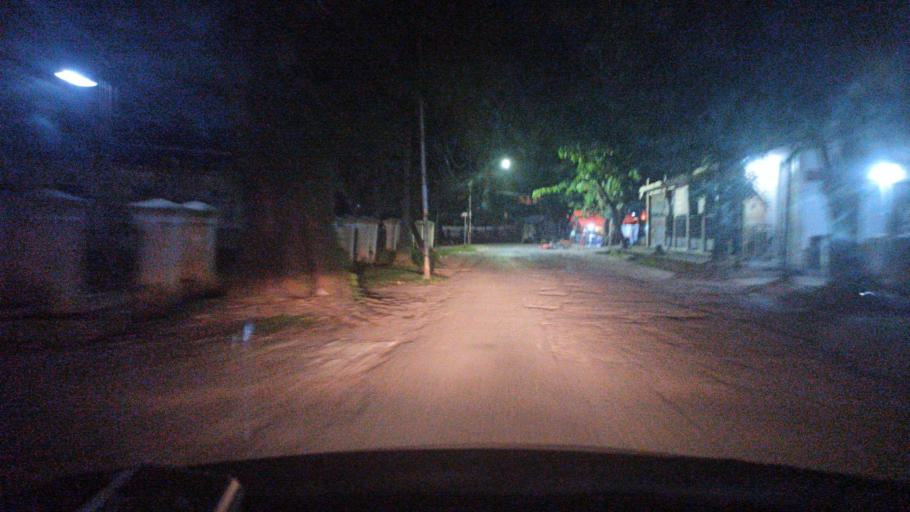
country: ID
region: South Sumatra
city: Plaju
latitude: -2.9917
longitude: 104.7486
